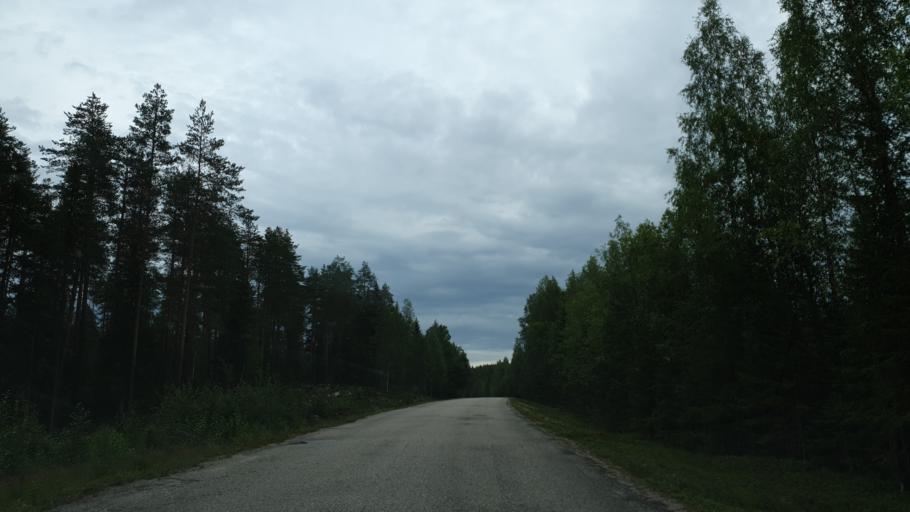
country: FI
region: Kainuu
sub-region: Kehys-Kainuu
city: Kuhmo
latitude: 64.3520
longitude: 29.1574
